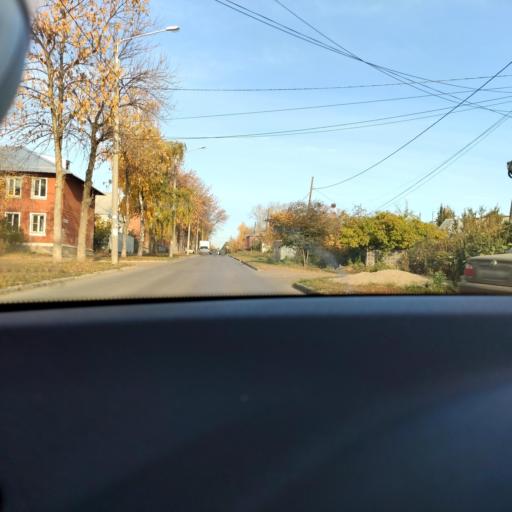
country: RU
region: Samara
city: Samara
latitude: 53.2291
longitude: 50.2397
